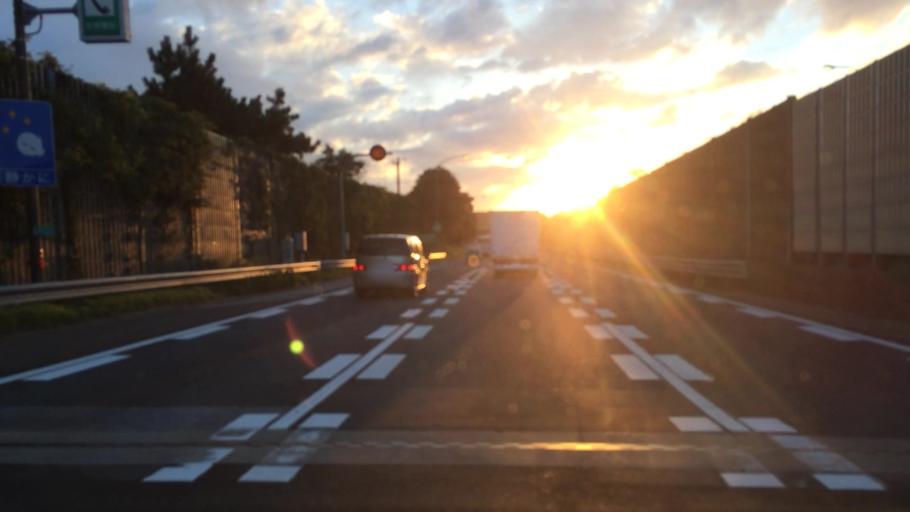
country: JP
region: Chiba
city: Chiba
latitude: 35.6550
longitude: 140.0953
